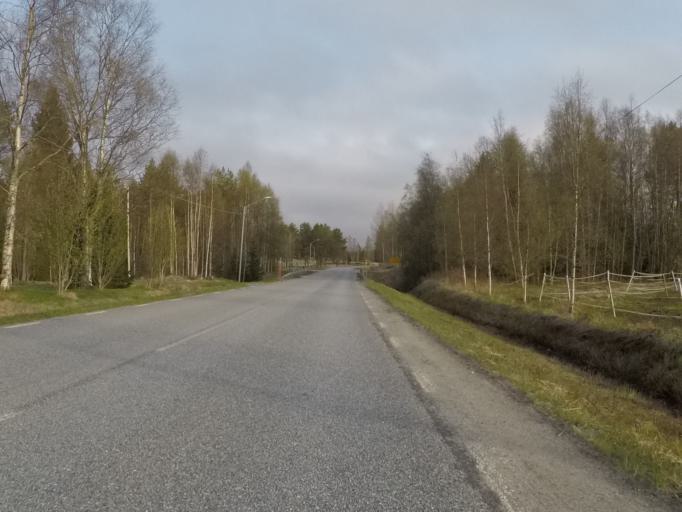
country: SE
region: Vaesterbotten
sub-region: Robertsfors Kommun
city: Robertsfors
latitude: 63.9686
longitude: 20.8123
